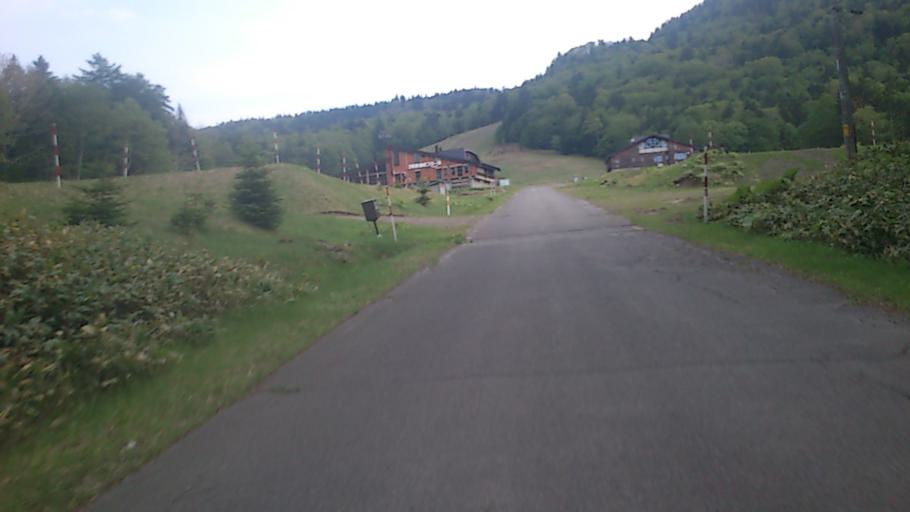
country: JP
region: Hokkaido
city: Bihoro
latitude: 43.4261
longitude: 144.0851
